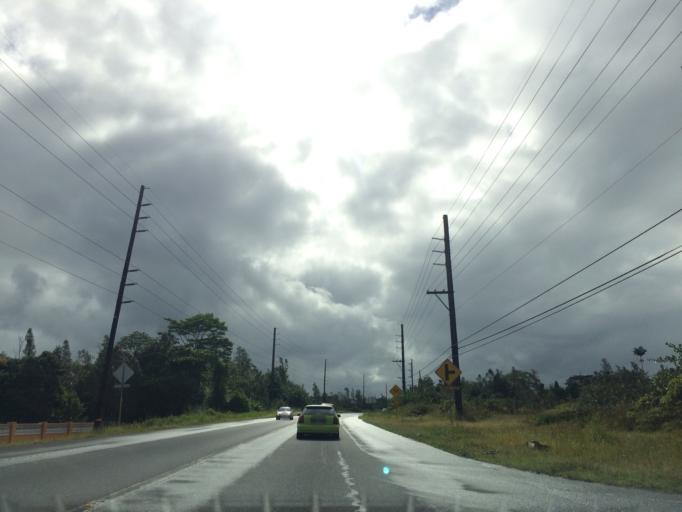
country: US
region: Hawaii
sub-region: Hawaii County
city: Ainaloa
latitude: 19.5456
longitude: -154.9770
